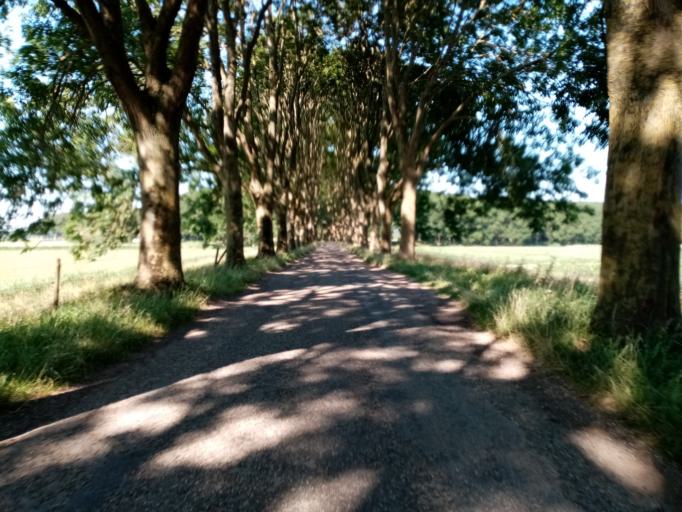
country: NL
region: North Brabant
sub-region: Gemeente Moerdijk
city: Klundert
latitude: 51.6802
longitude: 4.6389
